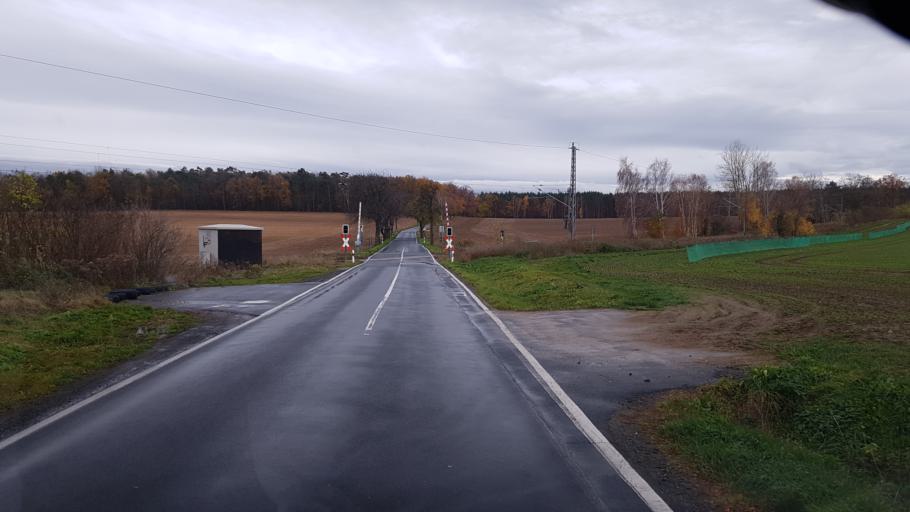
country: DE
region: Brandenburg
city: Ortrand
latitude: 51.3581
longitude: 13.7451
